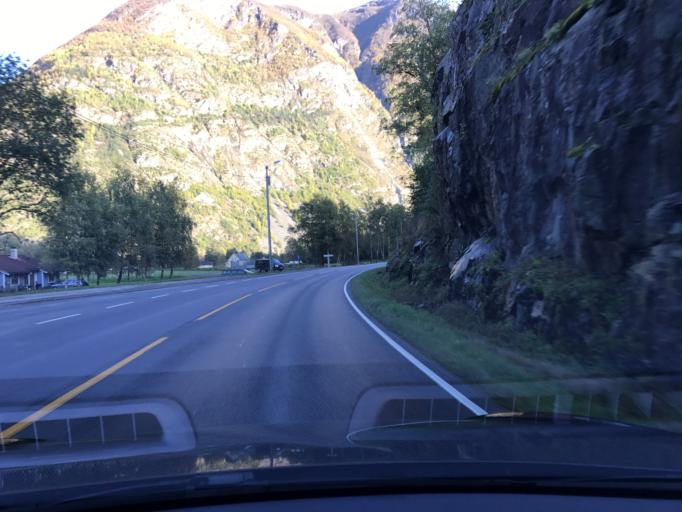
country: NO
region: Sogn og Fjordane
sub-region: Laerdal
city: Laerdalsoyri
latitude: 61.1006
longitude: 7.5075
